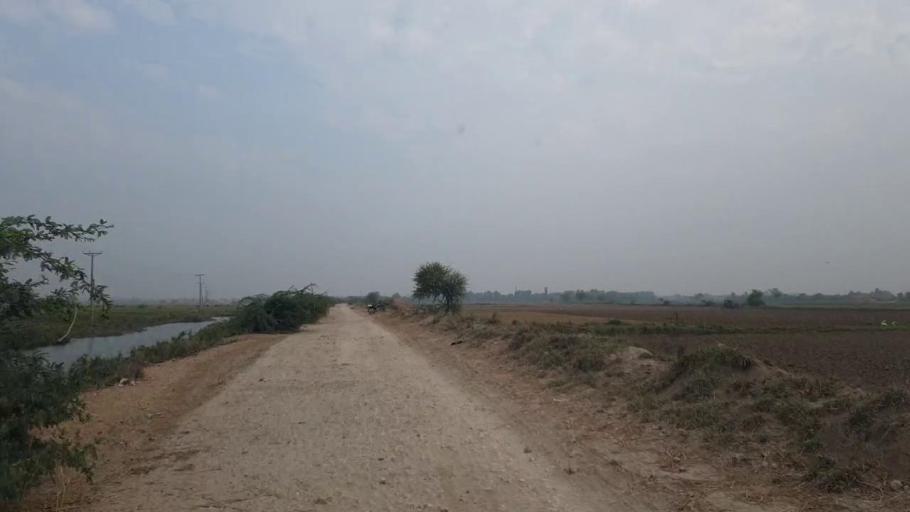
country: PK
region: Sindh
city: Talhar
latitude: 24.8208
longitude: 68.8778
